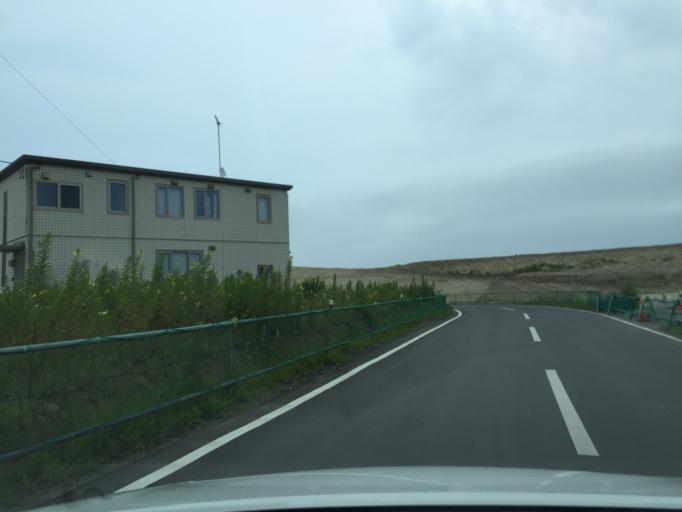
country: JP
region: Fukushima
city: Iwaki
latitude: 36.9920
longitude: 140.9706
